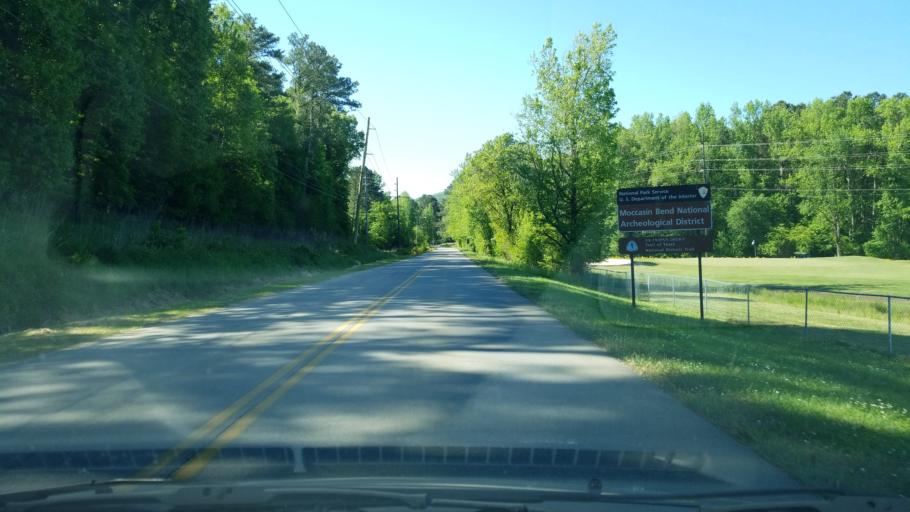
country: US
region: Tennessee
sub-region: Hamilton County
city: Chattanooga
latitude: 35.0429
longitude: -85.3337
